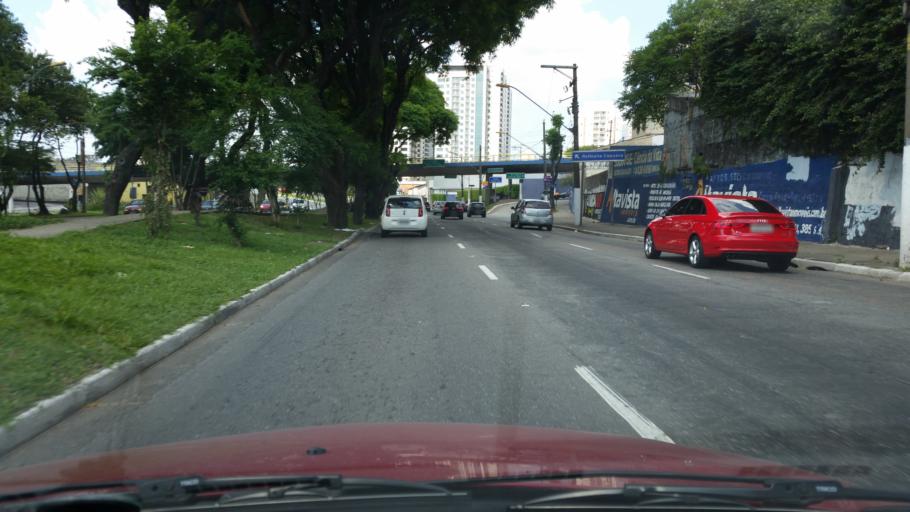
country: BR
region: Sao Paulo
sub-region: Santo Andre
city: Santo Andre
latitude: -23.6439
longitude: -46.5403
